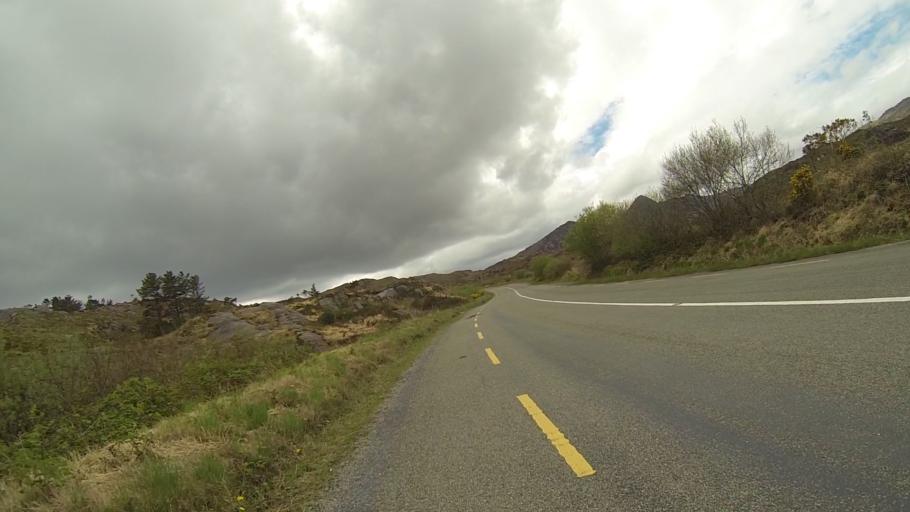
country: IE
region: Munster
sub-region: County Cork
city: Bantry
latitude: 51.7252
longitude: -9.5743
